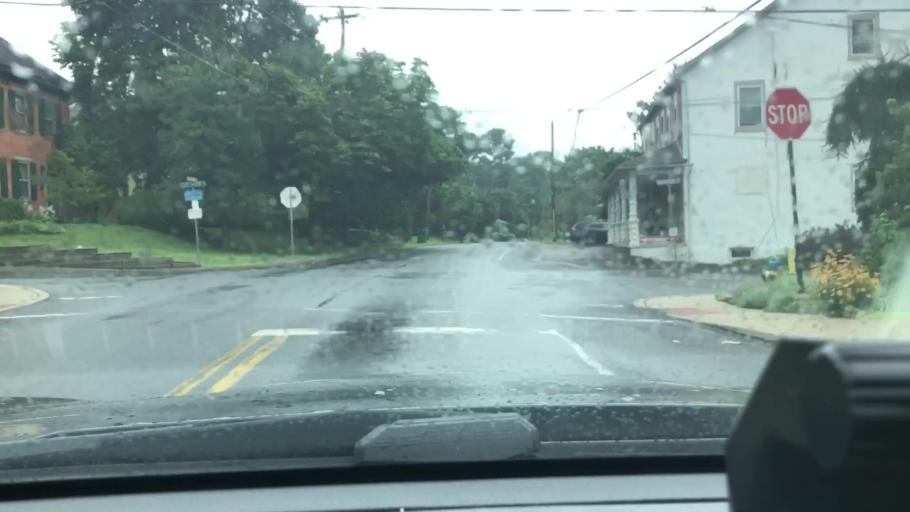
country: US
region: Pennsylvania
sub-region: Bucks County
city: Spinnerstown
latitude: 40.4389
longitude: -75.4370
